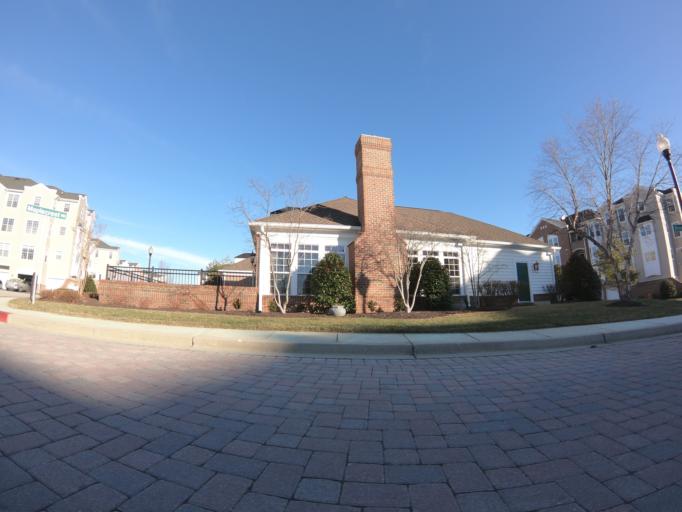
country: US
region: Maryland
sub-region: Howard County
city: West Elkridge
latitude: 39.2038
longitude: -76.7637
